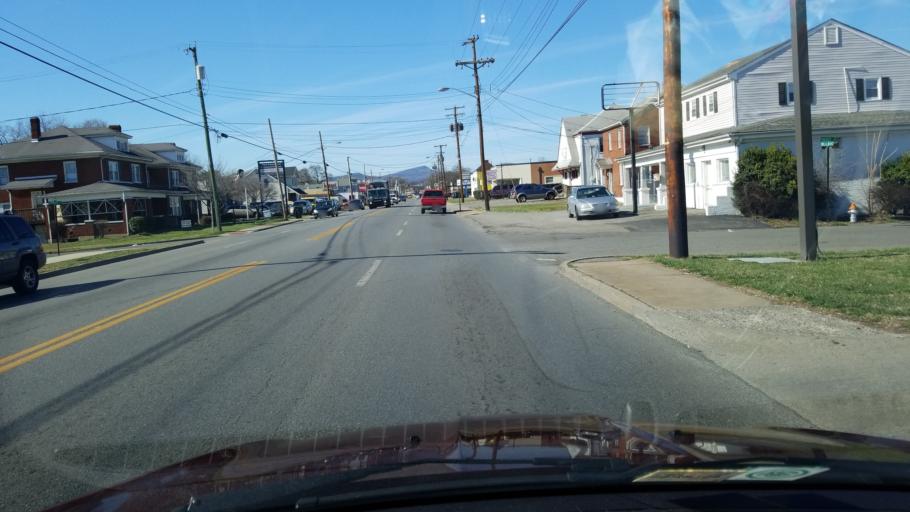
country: US
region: Virginia
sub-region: City of Roanoke
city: Roanoke
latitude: 37.2984
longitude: -79.9396
